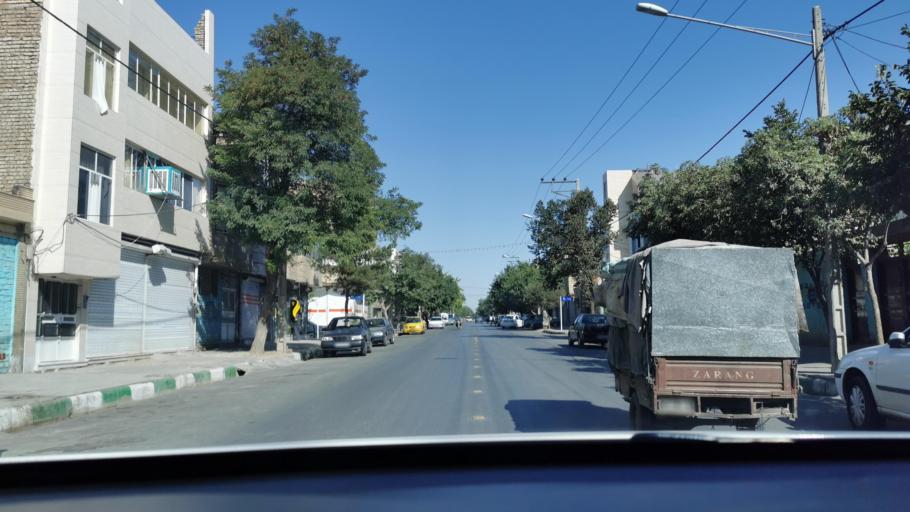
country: IR
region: Razavi Khorasan
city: Mashhad
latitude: 36.3354
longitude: 59.6375
